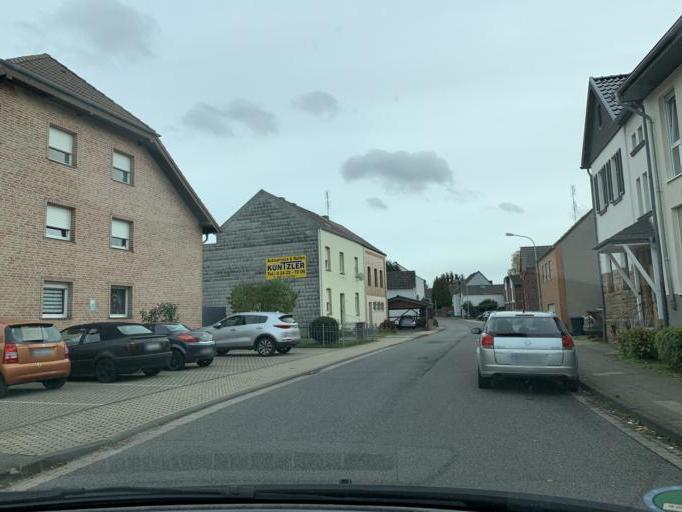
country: DE
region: North Rhine-Westphalia
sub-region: Regierungsbezirk Koln
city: Kreuzau
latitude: 50.7333
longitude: 6.5112
